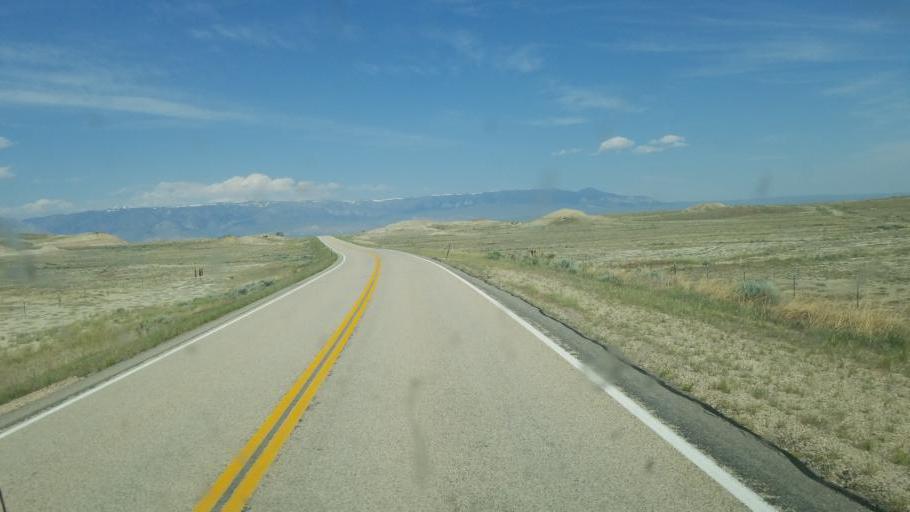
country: US
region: Wyoming
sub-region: Park County
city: Powell
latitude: 44.8410
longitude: -108.9890
